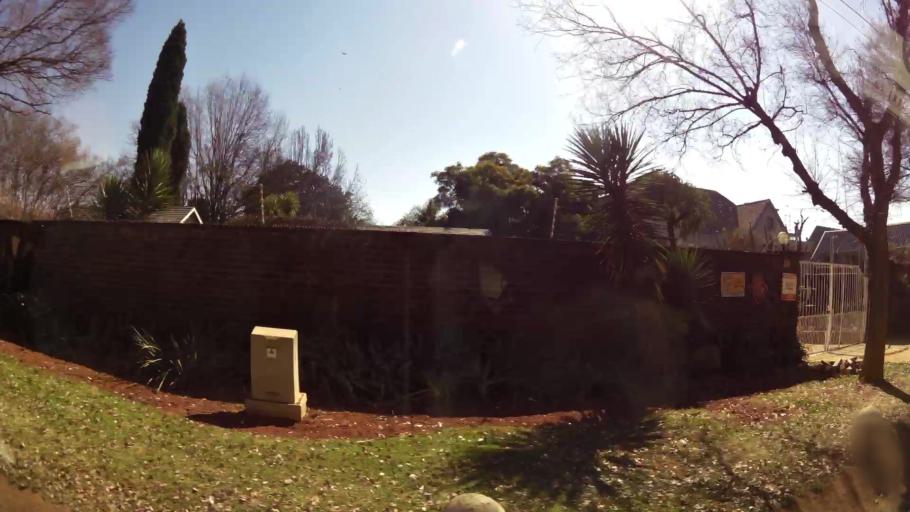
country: ZA
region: Gauteng
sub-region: City of Johannesburg Metropolitan Municipality
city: Modderfontein
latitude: -26.1390
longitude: 28.1036
